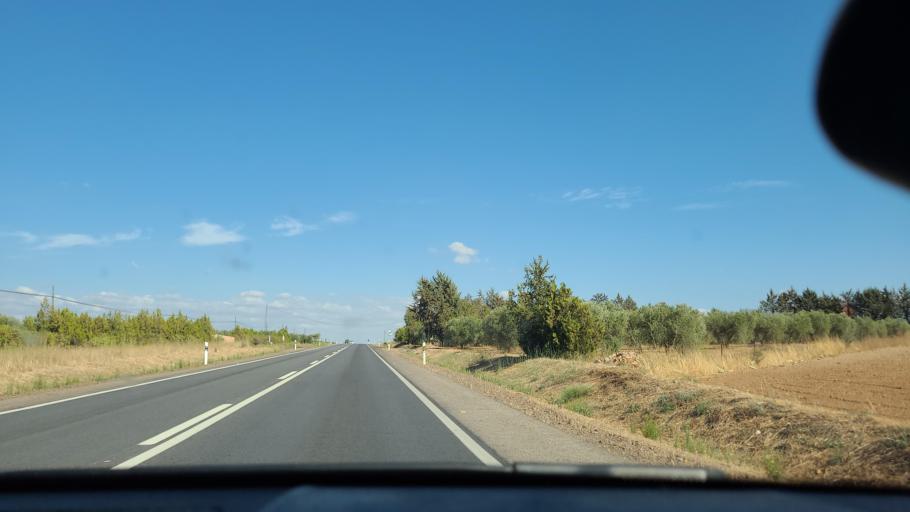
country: ES
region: Extremadura
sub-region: Provincia de Badajoz
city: Puebla de Sancho Perez
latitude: 38.4066
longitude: -6.3699
